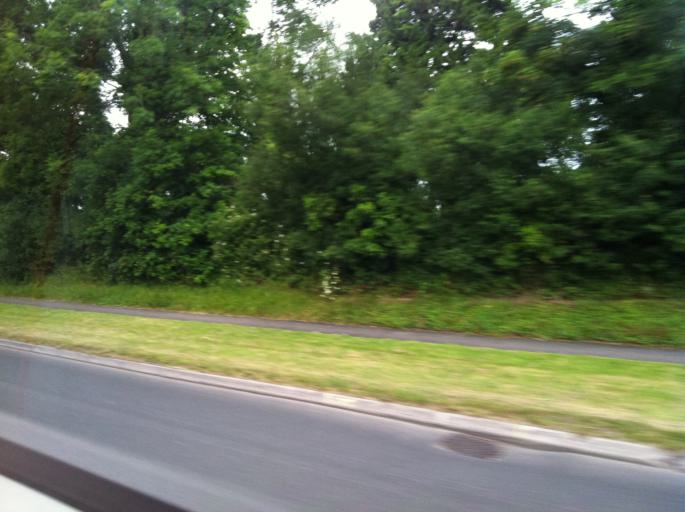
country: GB
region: Wales
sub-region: Vale of Glamorgan
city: Barry
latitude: 51.4387
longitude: -3.2640
